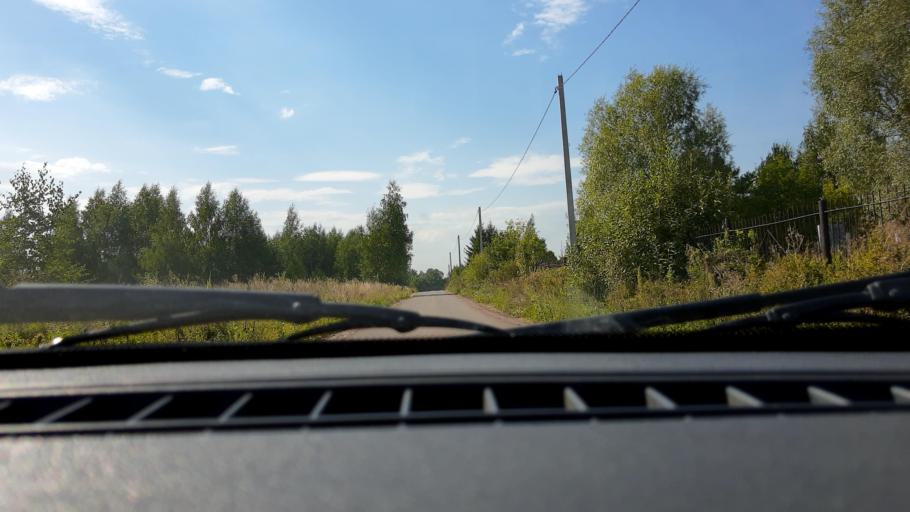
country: RU
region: Bashkortostan
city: Ufa
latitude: 54.8485
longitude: 56.1603
